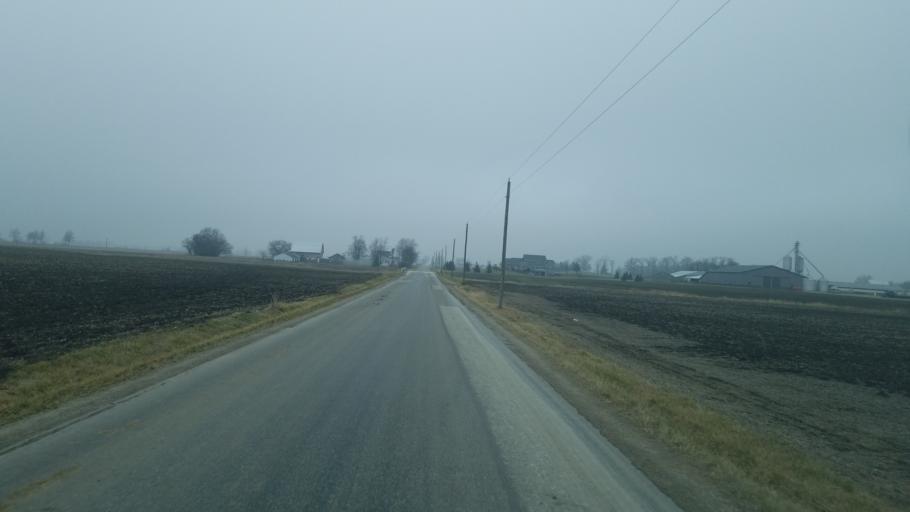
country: US
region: Indiana
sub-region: Adams County
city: Berne
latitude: 40.7112
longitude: -84.9751
